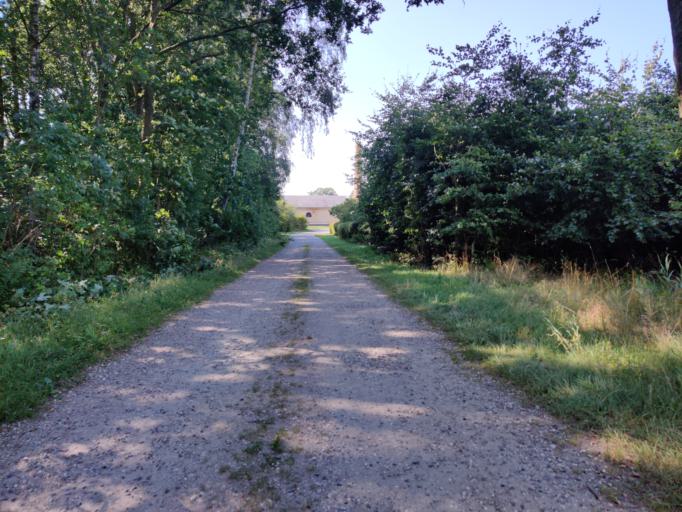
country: DK
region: Zealand
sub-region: Guldborgsund Kommune
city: Nykobing Falster
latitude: 54.6821
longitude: 11.9106
